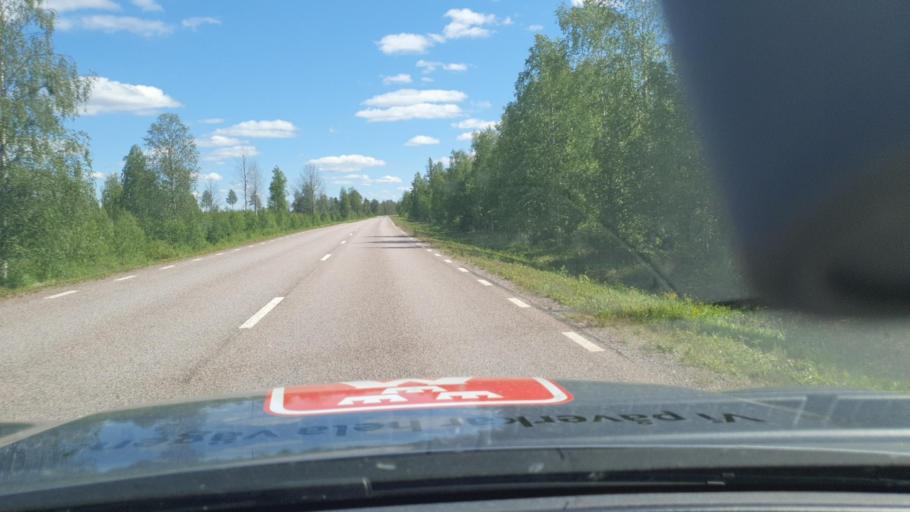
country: SE
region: Norrbotten
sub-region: Pajala Kommun
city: Pajala
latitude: 67.1981
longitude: 23.4397
